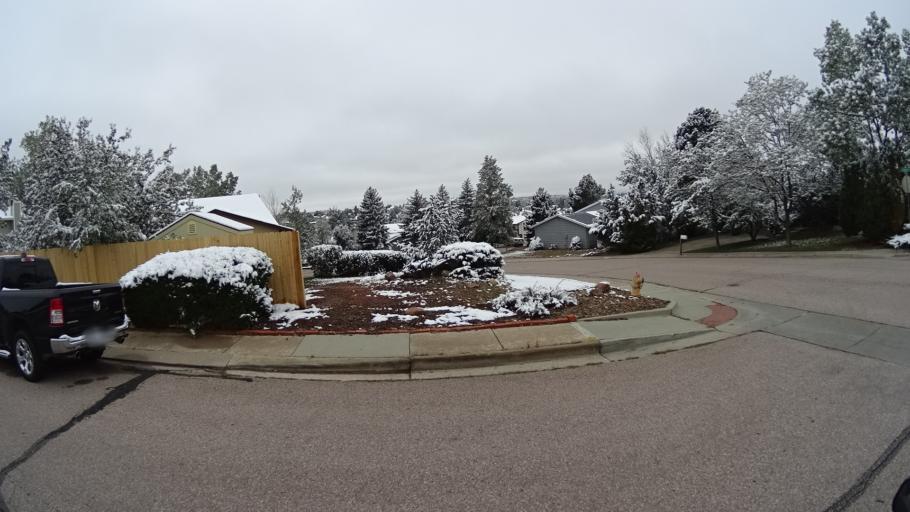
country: US
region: Colorado
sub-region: El Paso County
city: Colorado Springs
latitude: 38.9234
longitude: -104.7873
